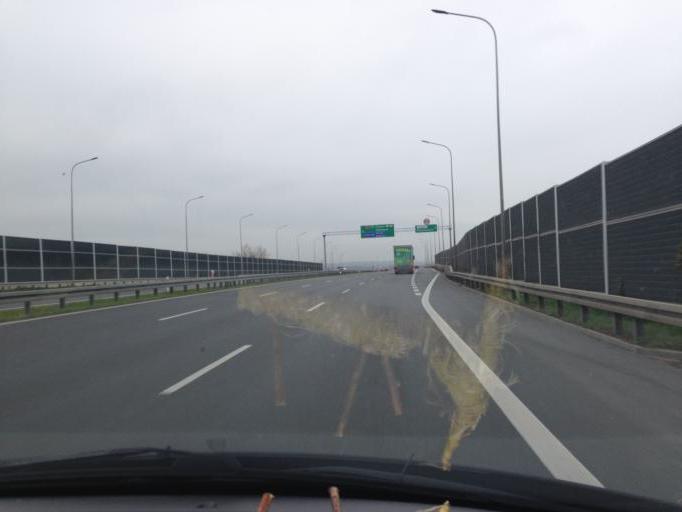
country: PL
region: Lesser Poland Voivodeship
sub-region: Powiat wielicki
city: Kokotow
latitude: 50.0423
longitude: 20.0679
